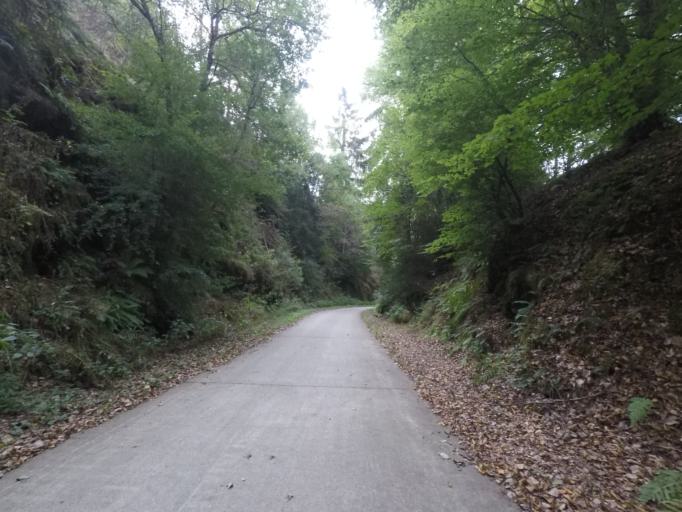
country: BE
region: Wallonia
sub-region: Province du Luxembourg
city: Martelange
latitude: 49.8233
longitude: 5.7544
